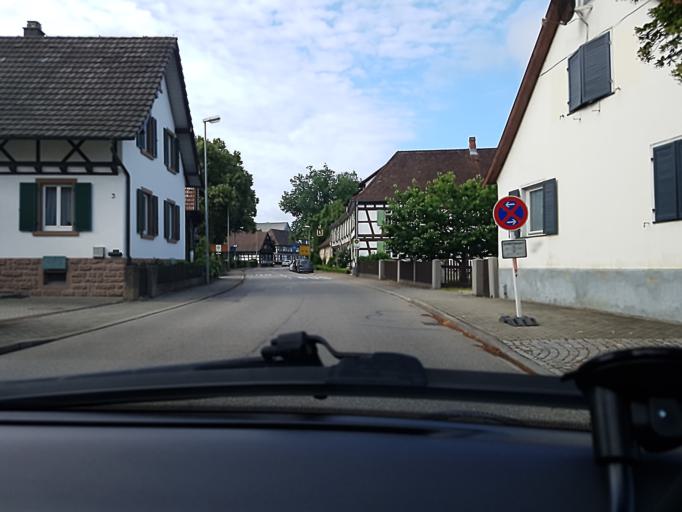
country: DE
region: Baden-Wuerttemberg
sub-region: Freiburg Region
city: Willstatt
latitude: 48.5661
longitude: 7.8692
